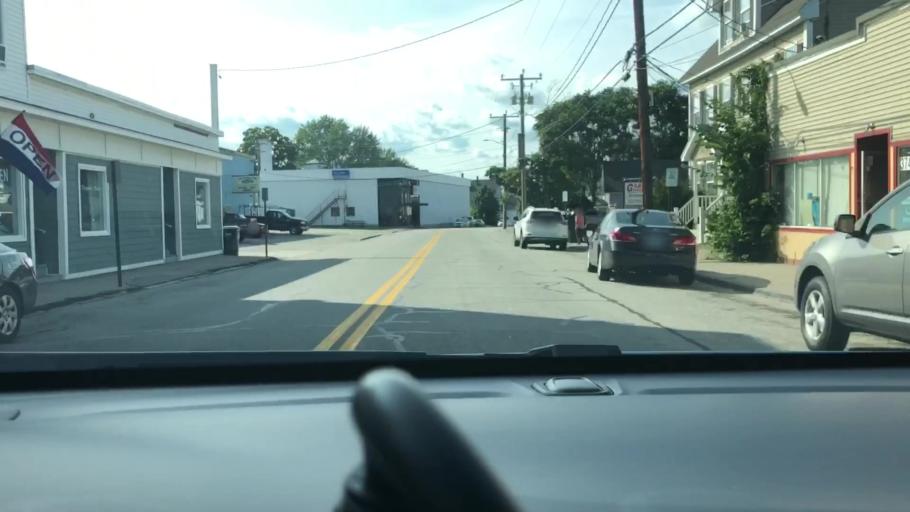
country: US
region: New Hampshire
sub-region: Hillsborough County
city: Manchester
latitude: 42.9829
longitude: -71.4401
